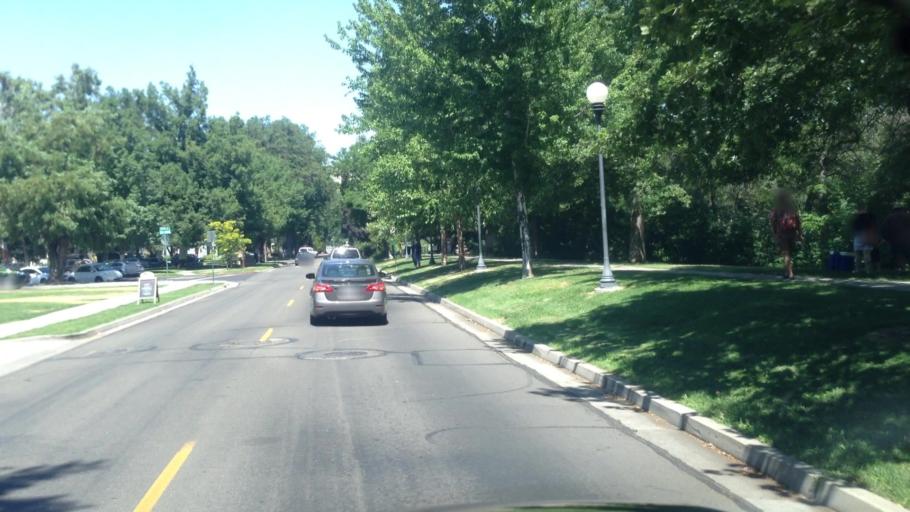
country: US
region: Nevada
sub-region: Washoe County
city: Reno
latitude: 39.5217
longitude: -119.8220
